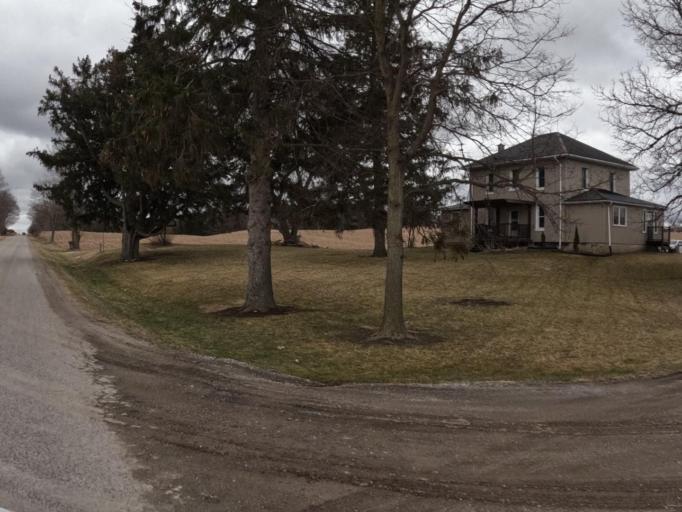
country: CA
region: Ontario
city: Dorchester
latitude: 42.9782
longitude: -80.9718
